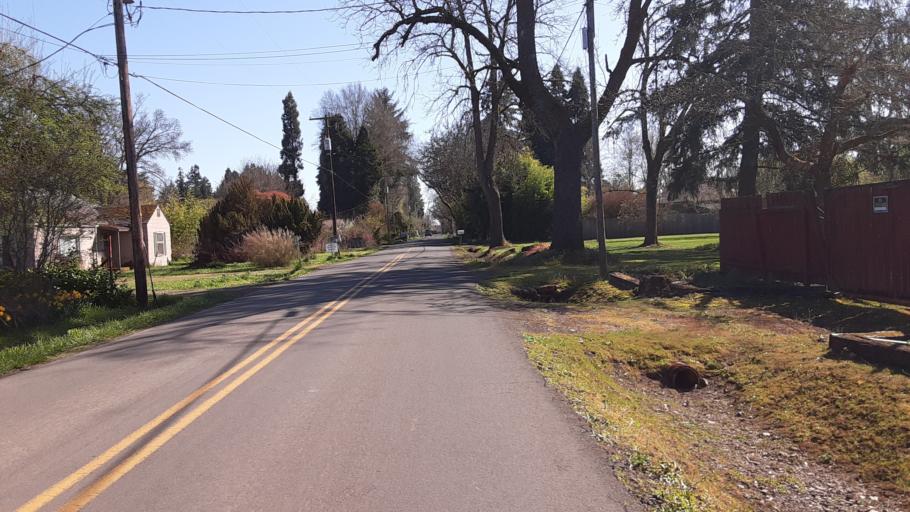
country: US
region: Oregon
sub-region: Benton County
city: Corvallis
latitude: 44.5440
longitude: -123.2556
